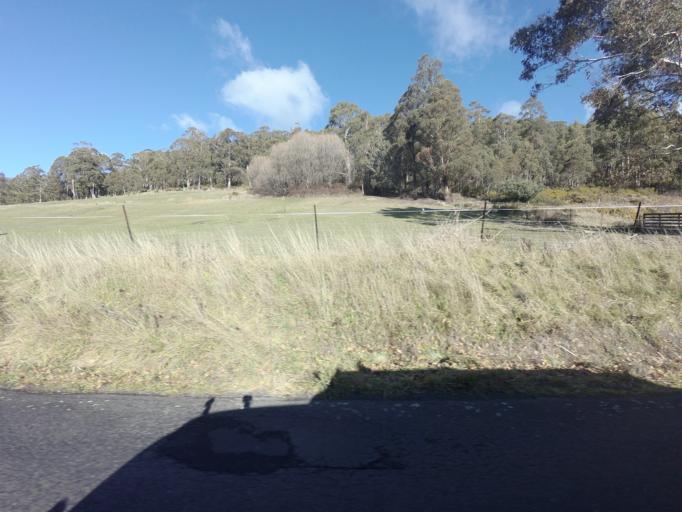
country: AU
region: Tasmania
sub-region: Glenorchy
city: Berriedale
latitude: -42.8418
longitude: 147.1872
